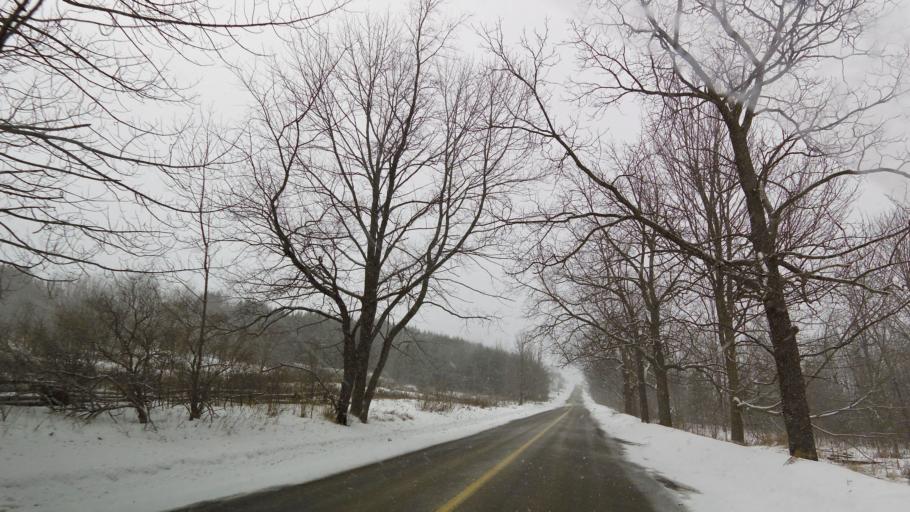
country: CA
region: Ontario
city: Orangeville
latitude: 43.8935
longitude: -80.0657
